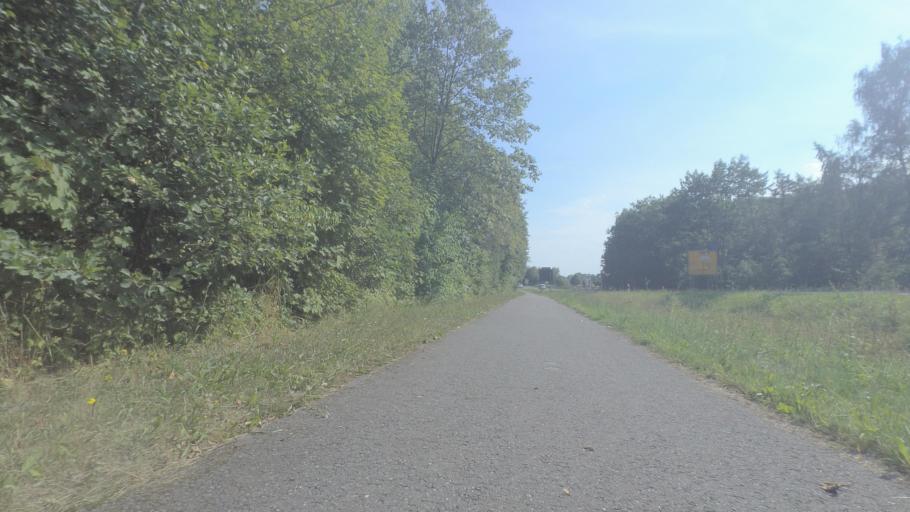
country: DE
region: Mecklenburg-Vorpommern
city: Grimmen
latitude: 54.1100
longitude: 13.0588
